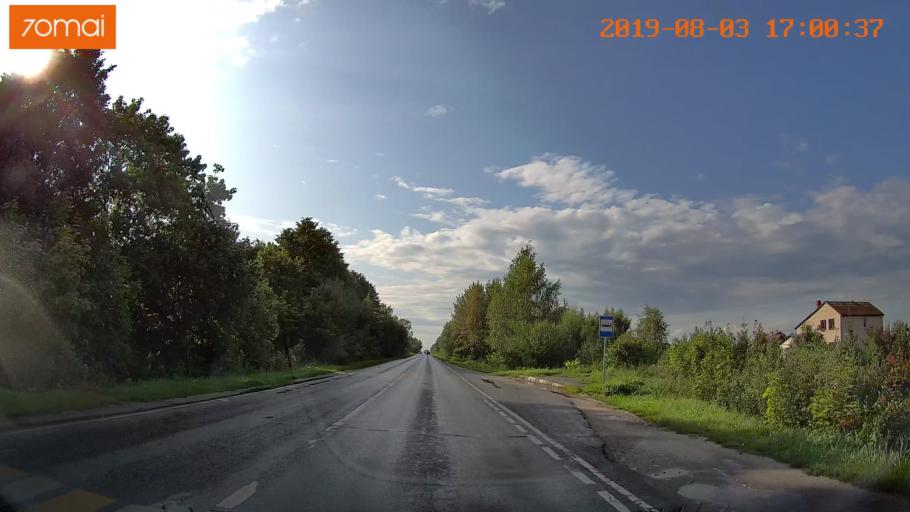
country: RU
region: Moskovskaya
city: Voskresensk
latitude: 55.3384
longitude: 38.6156
